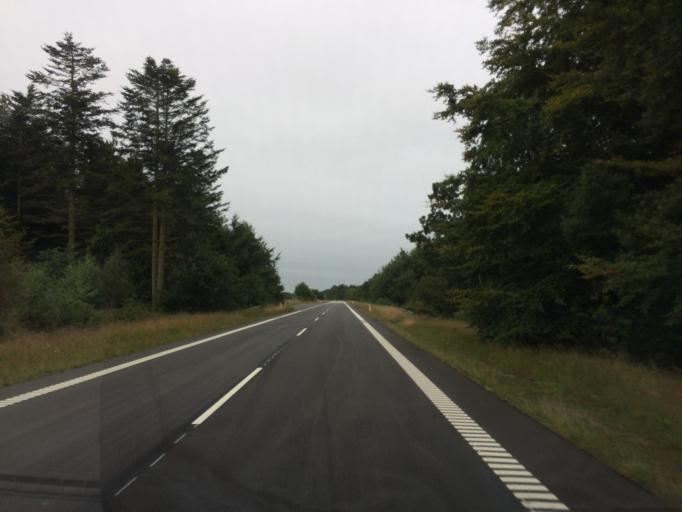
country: DK
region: Central Jutland
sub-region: Herning Kommune
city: Lind
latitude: 56.0253
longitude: 8.9963
